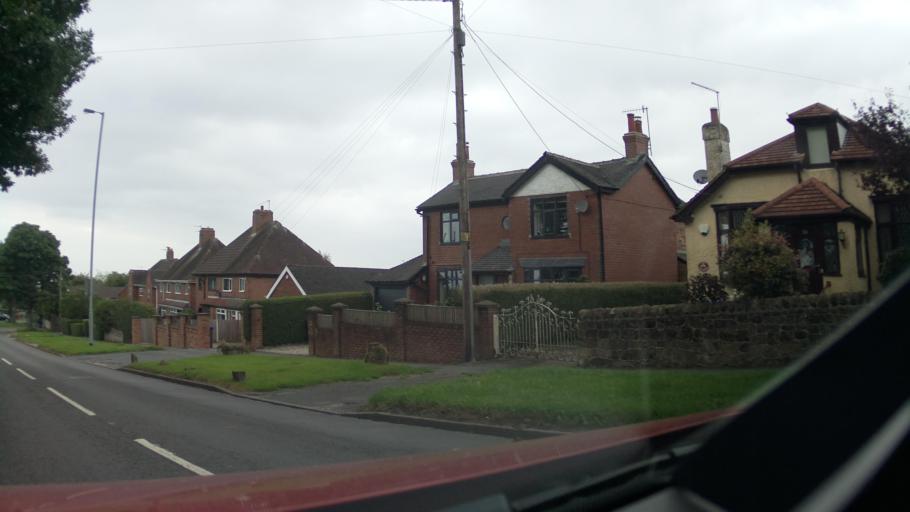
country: GB
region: England
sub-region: Staffordshire
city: Longton
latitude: 53.0236
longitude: -2.0921
